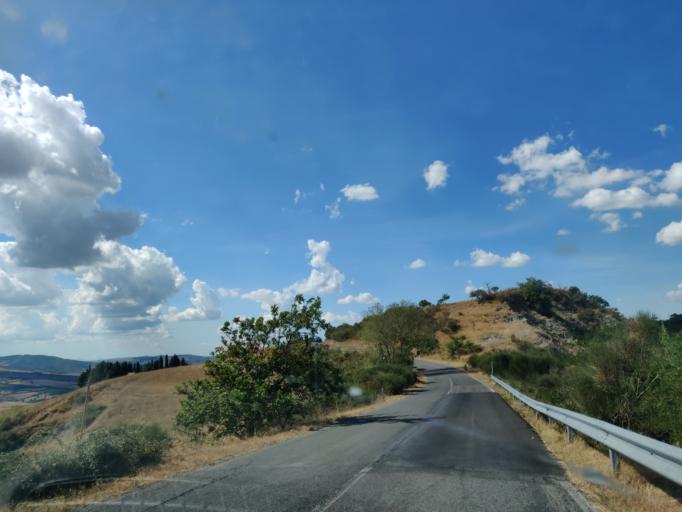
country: IT
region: Tuscany
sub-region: Provincia di Siena
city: Radicofani
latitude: 42.9539
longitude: 11.7281
